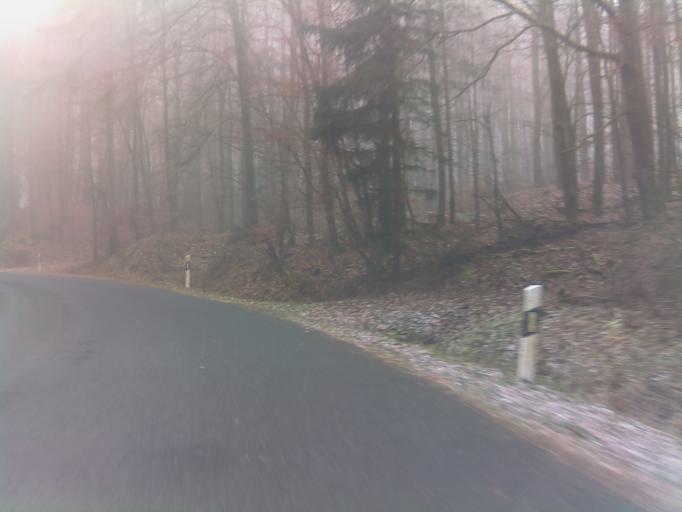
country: DE
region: Bavaria
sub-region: Regierungsbezirk Unterfranken
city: Burgpreppach
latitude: 50.0944
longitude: 10.5900
